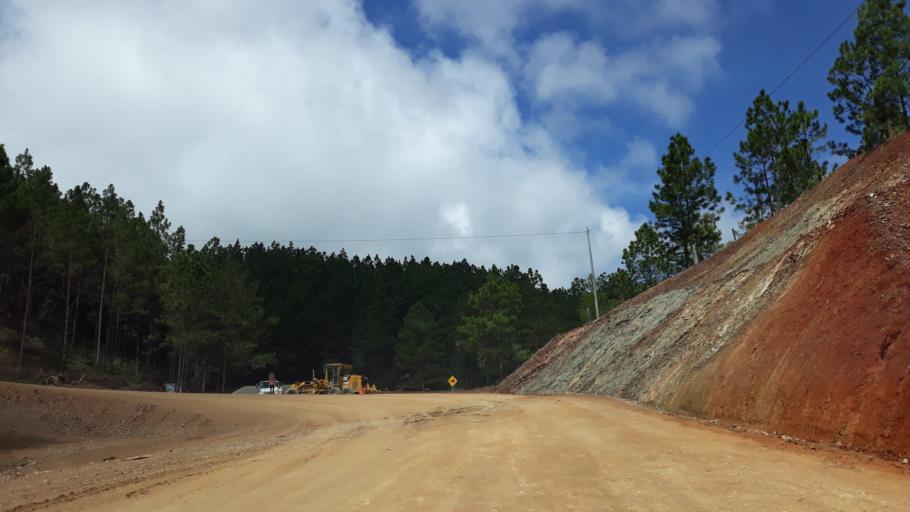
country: HN
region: El Paraiso
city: Santa Cruz
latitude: 13.7683
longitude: -86.6415
